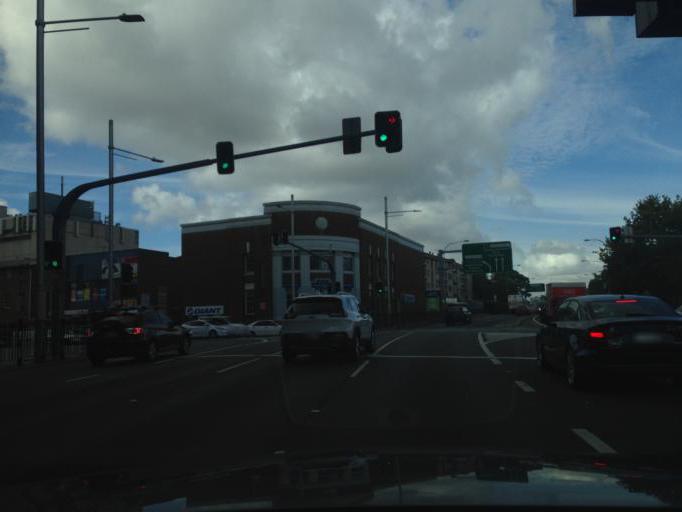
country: AU
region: New South Wales
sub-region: Ryde
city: Denistone
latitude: -33.8125
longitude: 151.1052
